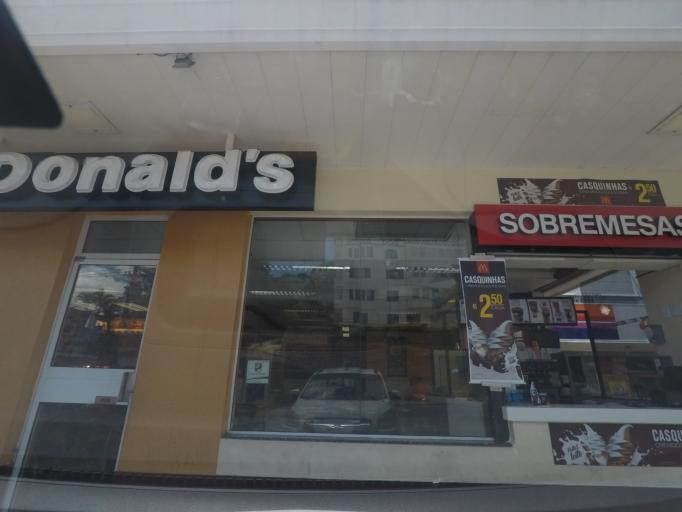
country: BR
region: Rio de Janeiro
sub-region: Petropolis
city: Petropolis
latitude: -22.5056
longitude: -43.1807
